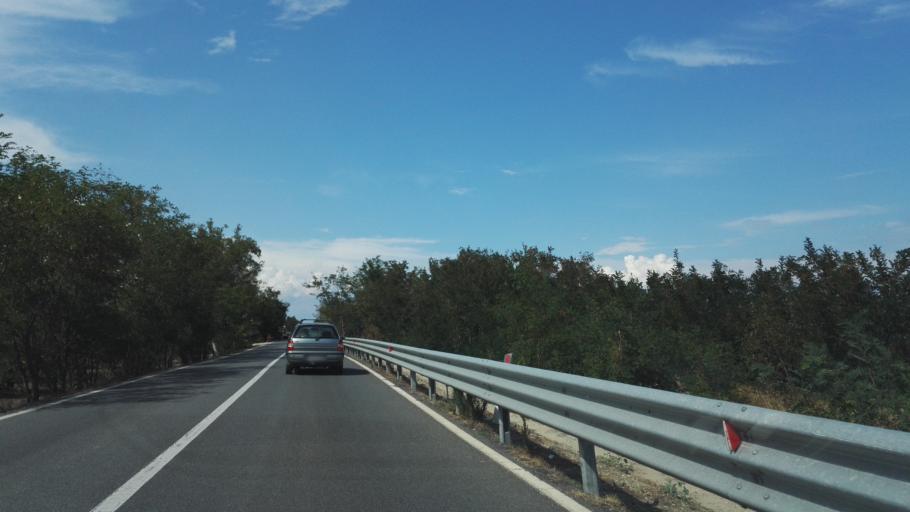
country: IT
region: Calabria
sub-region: Provincia di Catanzaro
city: Santa Caterina dello Ionio Marina
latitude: 38.5488
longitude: 16.5702
